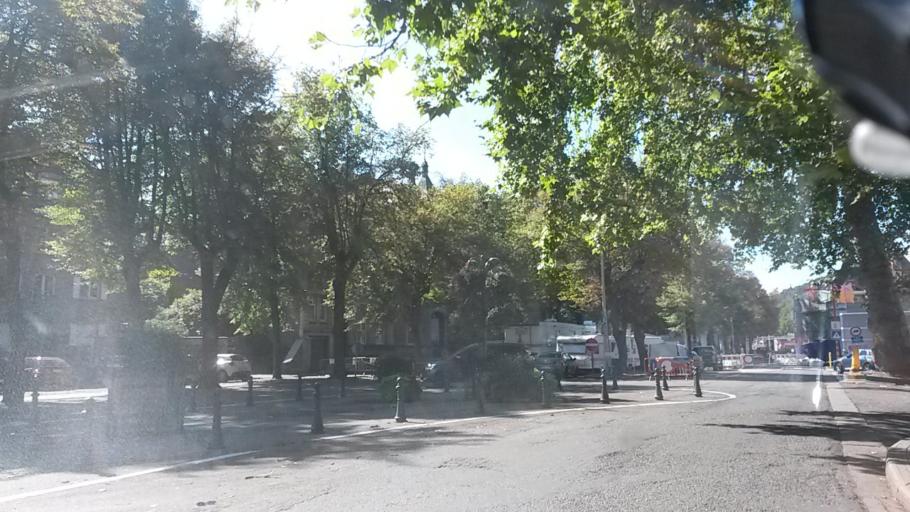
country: BE
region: Wallonia
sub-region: Province de Liege
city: Huy
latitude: 50.5250
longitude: 5.2432
